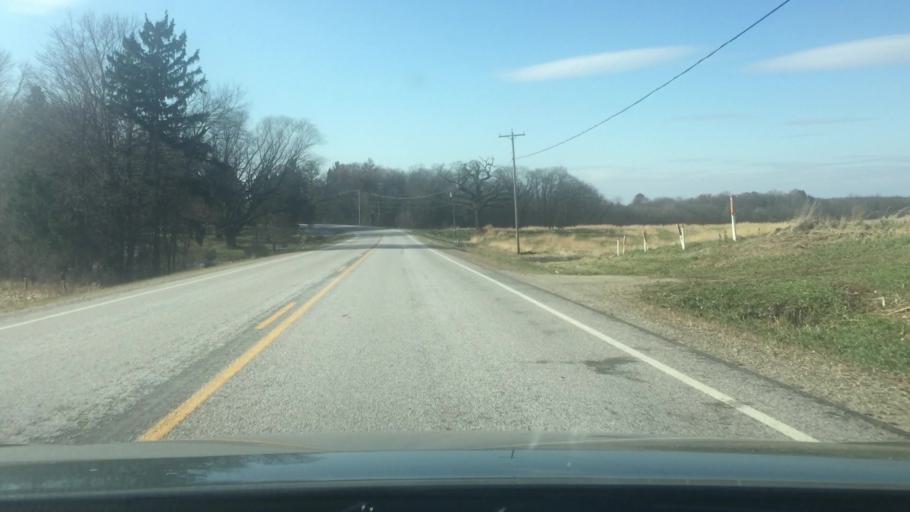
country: US
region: Wisconsin
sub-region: Jefferson County
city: Lake Koshkonong
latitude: 42.9488
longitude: -88.9047
